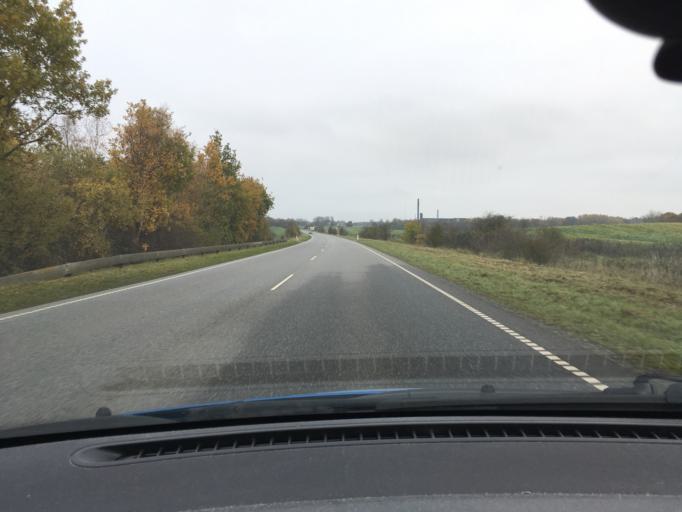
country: DK
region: South Denmark
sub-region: Aabenraa Kommune
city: Aabenraa
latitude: 54.9970
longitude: 9.4146
